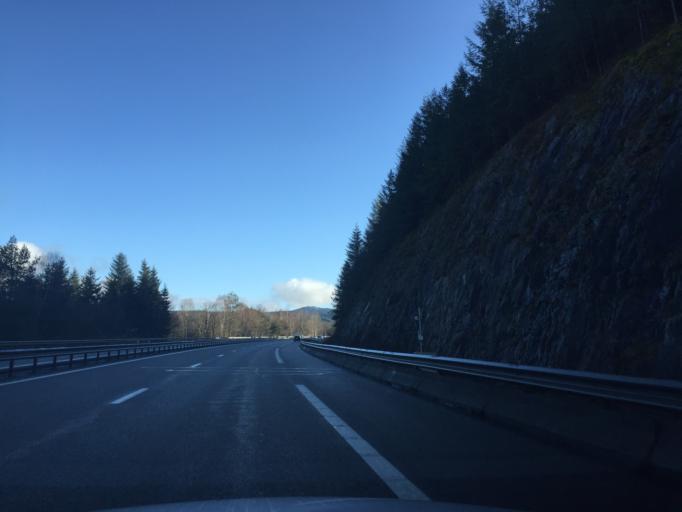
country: FR
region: Auvergne
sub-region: Departement du Puy-de-Dome
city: Chabreloche
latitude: 45.8765
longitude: 3.6911
